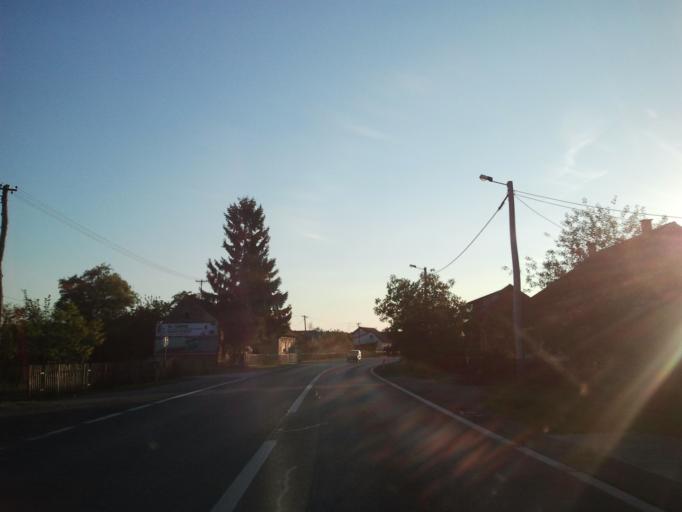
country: HR
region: Sisacko-Moslavacka
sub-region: Grad Sisak
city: Sisak
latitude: 45.4393
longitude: 16.3526
